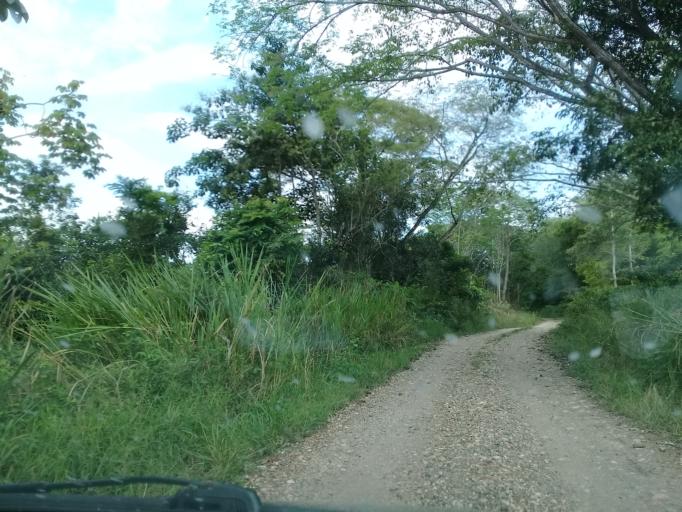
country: CO
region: Antioquia
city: Puerto Triunfo
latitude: 5.6966
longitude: -74.5550
